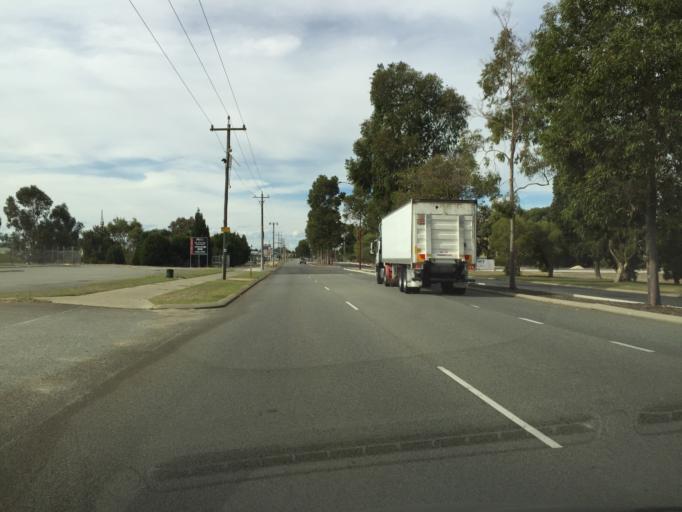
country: AU
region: Western Australia
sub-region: Canning
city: Canning Vale
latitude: -32.0647
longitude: 115.9016
